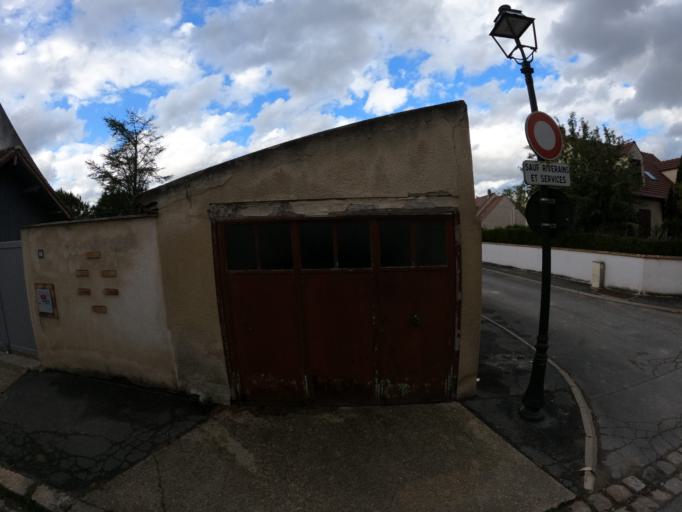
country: FR
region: Ile-de-France
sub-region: Departement de Seine-et-Marne
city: Coupvray
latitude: 48.8947
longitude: 2.7938
